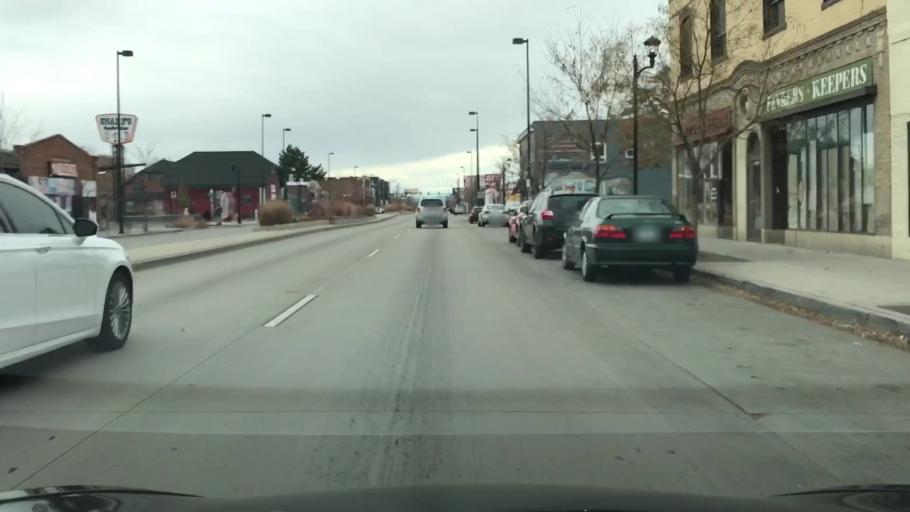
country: US
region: Colorado
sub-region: Arapahoe County
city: Englewood
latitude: 39.6902
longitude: -104.9876
